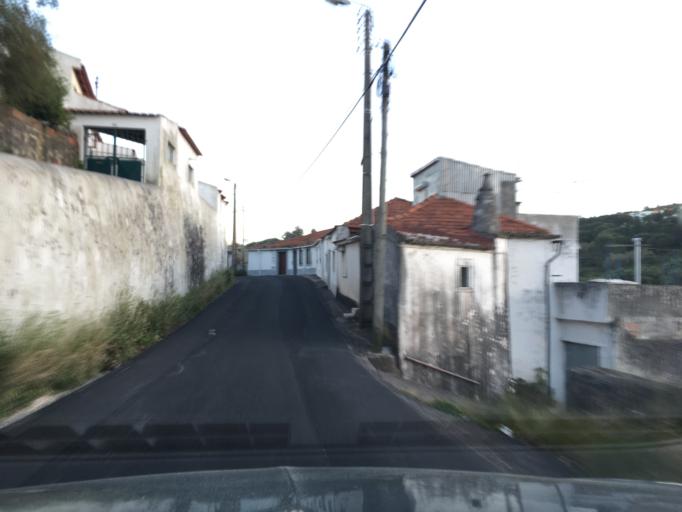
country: PT
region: Lisbon
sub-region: Oeiras
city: Quejas
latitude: 38.7207
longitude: -9.2764
